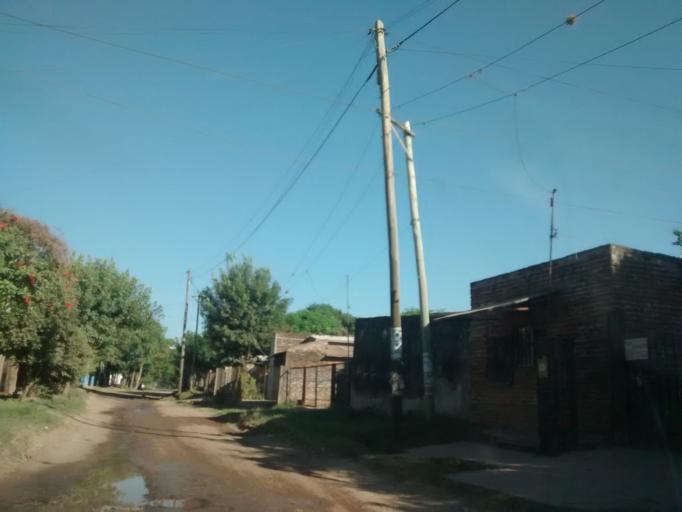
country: AR
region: Chaco
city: Resistencia
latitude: -27.4547
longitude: -58.9647
